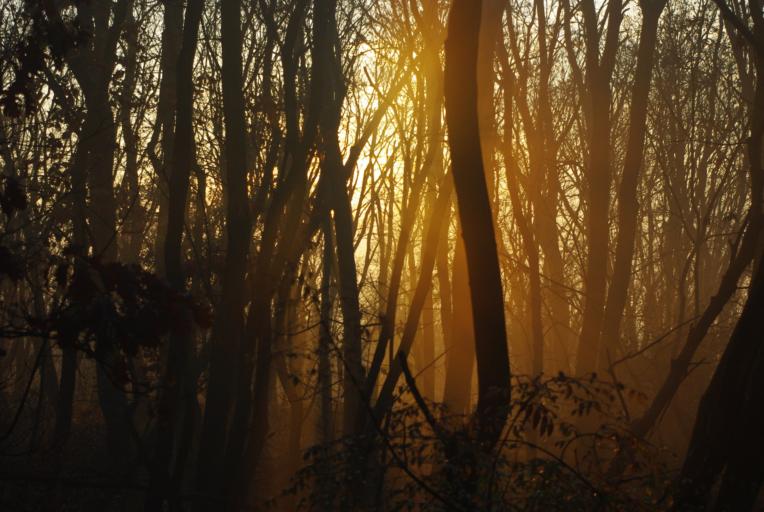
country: HU
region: Pest
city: Piliscsaba
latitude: 47.6345
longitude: 18.8640
